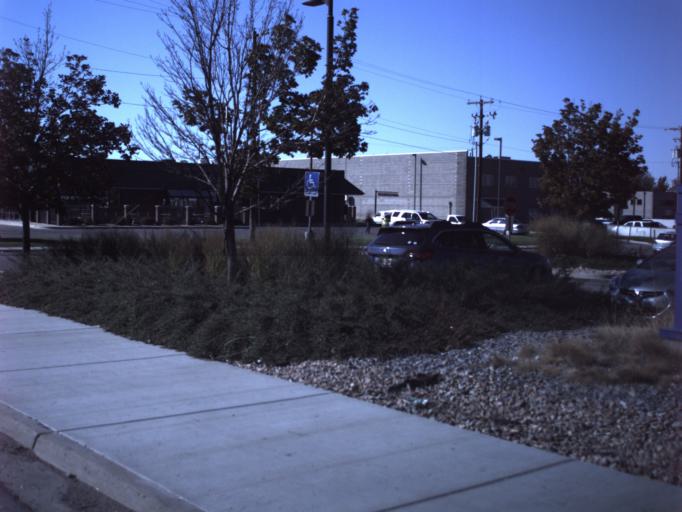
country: US
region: Utah
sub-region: Salt Lake County
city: Centerfield
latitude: 40.6999
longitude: -111.8973
